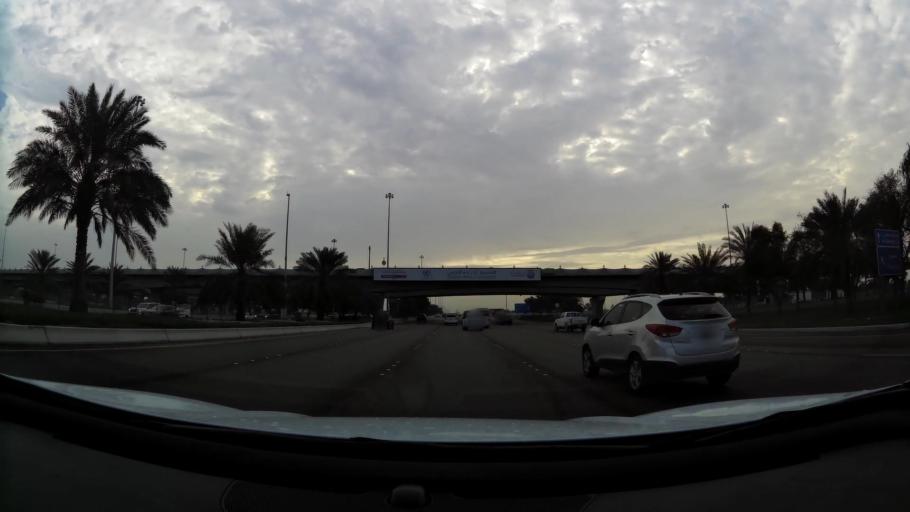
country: AE
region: Abu Dhabi
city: Abu Dhabi
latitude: 24.4059
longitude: 54.4767
